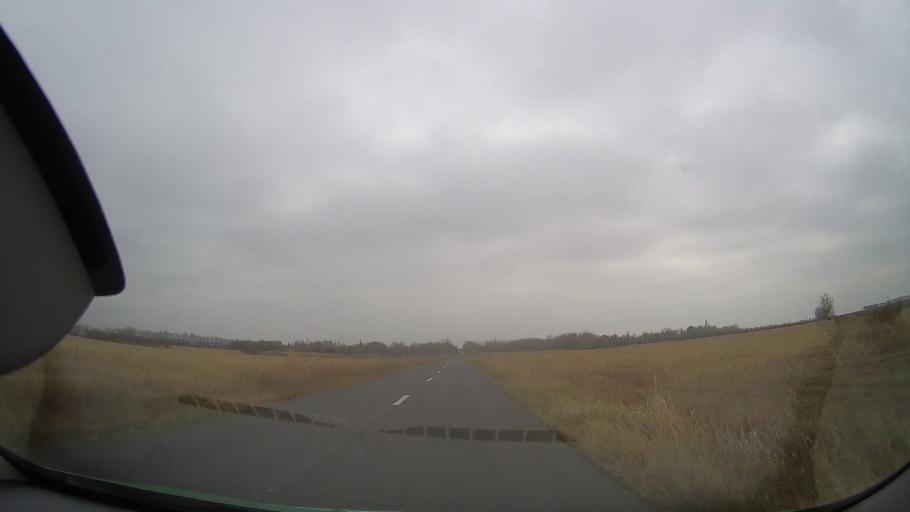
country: RO
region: Buzau
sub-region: Comuna Bradeanu
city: Bradeanu
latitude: 44.8868
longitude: 26.8752
